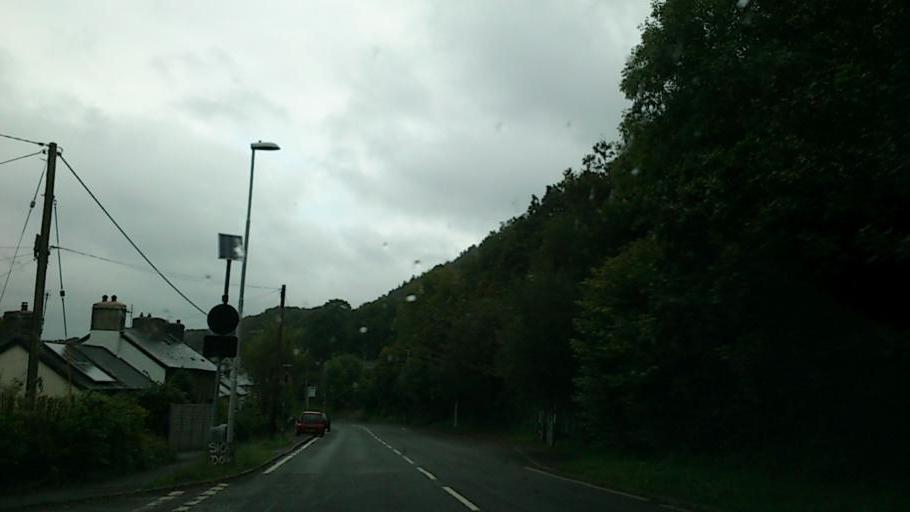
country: GB
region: Wales
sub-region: County of Ceredigion
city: Bow Street
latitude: 52.4990
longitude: -3.9844
